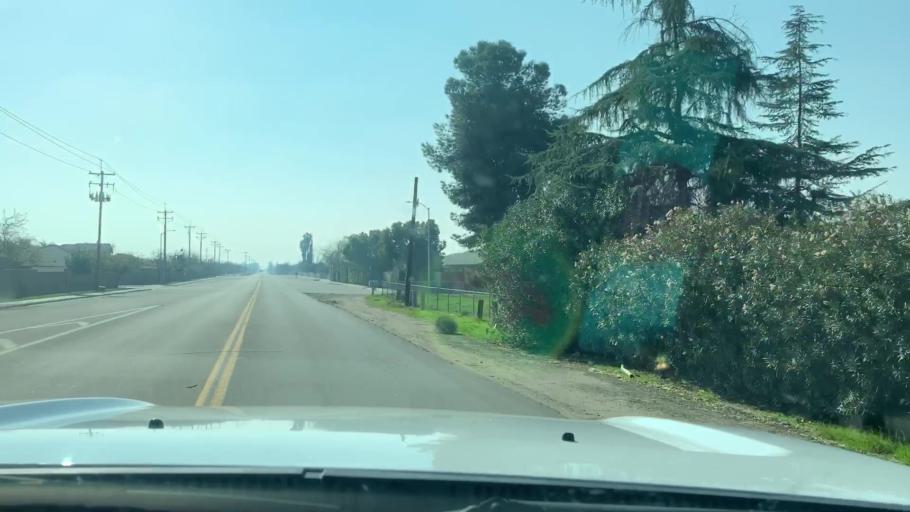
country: US
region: California
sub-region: Kern County
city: Shafter
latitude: 35.4924
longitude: -119.2785
